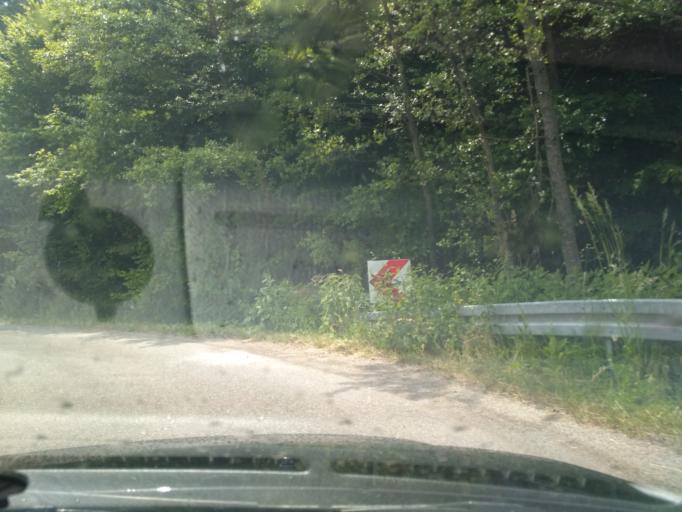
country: PL
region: Subcarpathian Voivodeship
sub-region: Powiat przeworski
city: Jawornik Polski
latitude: 49.9236
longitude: 22.2781
